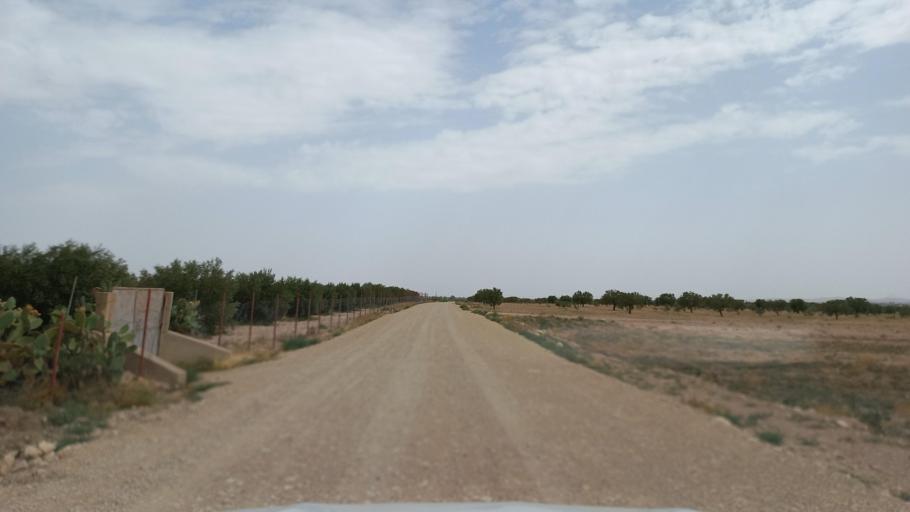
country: TN
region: Al Qasrayn
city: Kasserine
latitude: 35.2801
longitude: 9.0125
